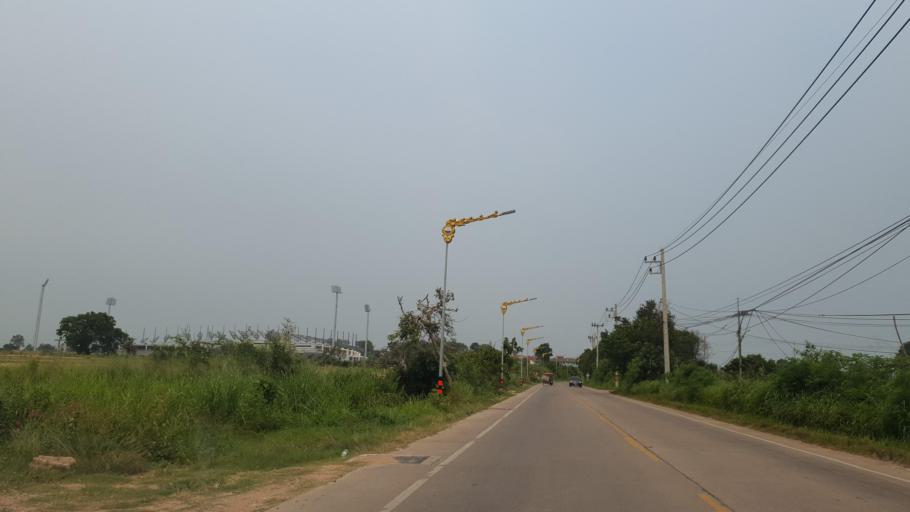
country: TH
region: Chon Buri
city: Phatthaya
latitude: 12.8936
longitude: 100.9269
